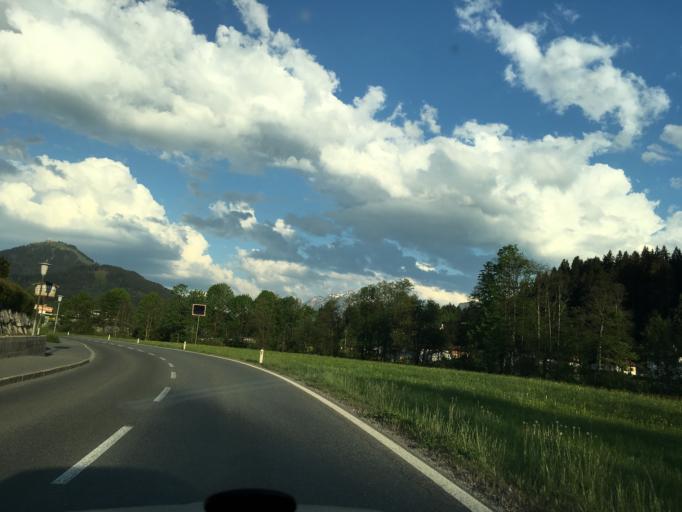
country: AT
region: Tyrol
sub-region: Politischer Bezirk Kitzbuhel
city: Fieberbrunn
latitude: 47.4914
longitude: 12.5163
